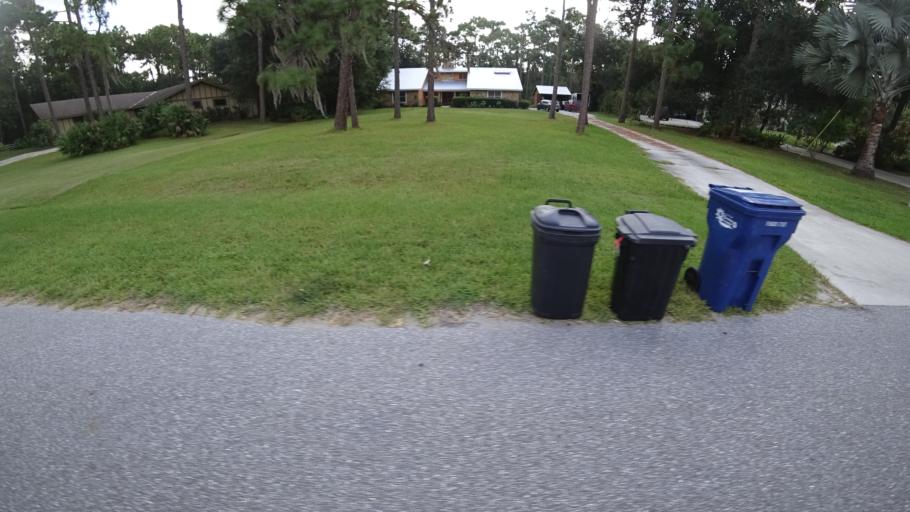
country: US
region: Florida
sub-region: Sarasota County
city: The Meadows
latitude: 27.4332
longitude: -82.4447
